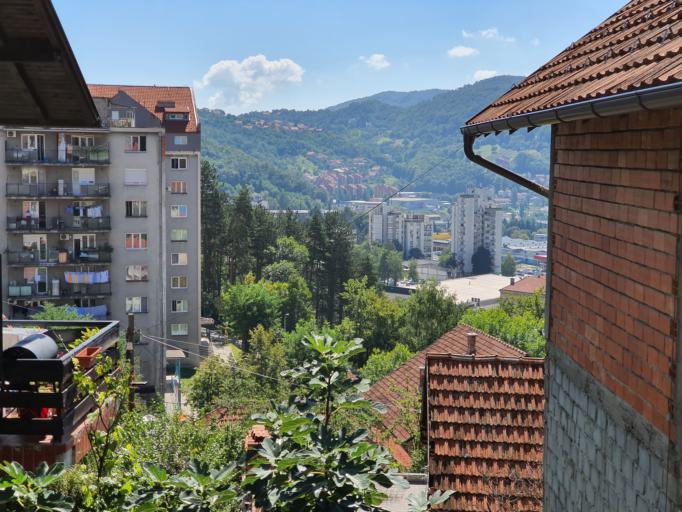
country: RS
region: Central Serbia
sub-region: Zlatiborski Okrug
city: Uzice
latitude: 43.8557
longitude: 19.8523
